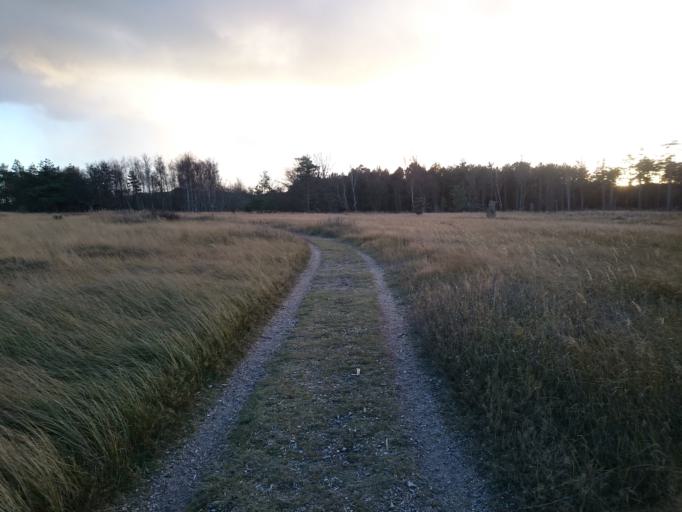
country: DK
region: North Denmark
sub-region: Frederikshavn Kommune
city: Skagen
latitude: 57.7028
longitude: 10.5421
